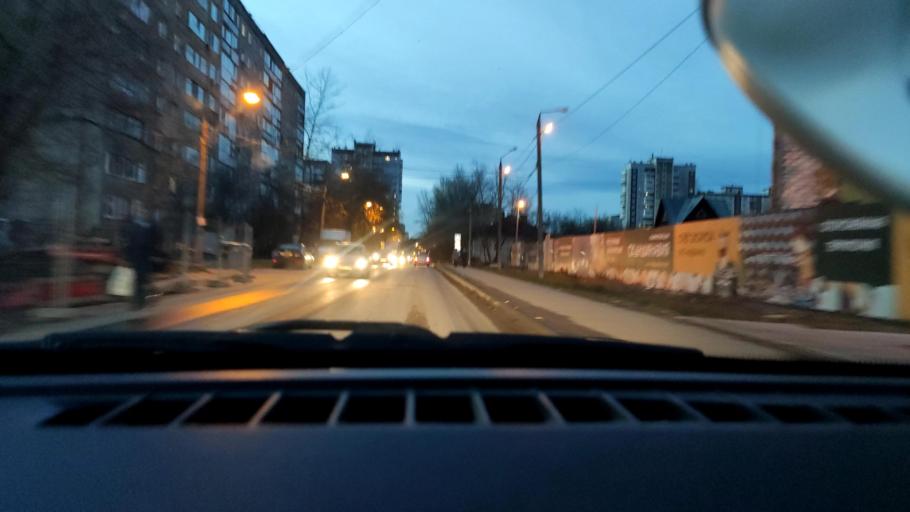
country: RU
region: Perm
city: Kondratovo
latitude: 58.0001
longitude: 56.1465
